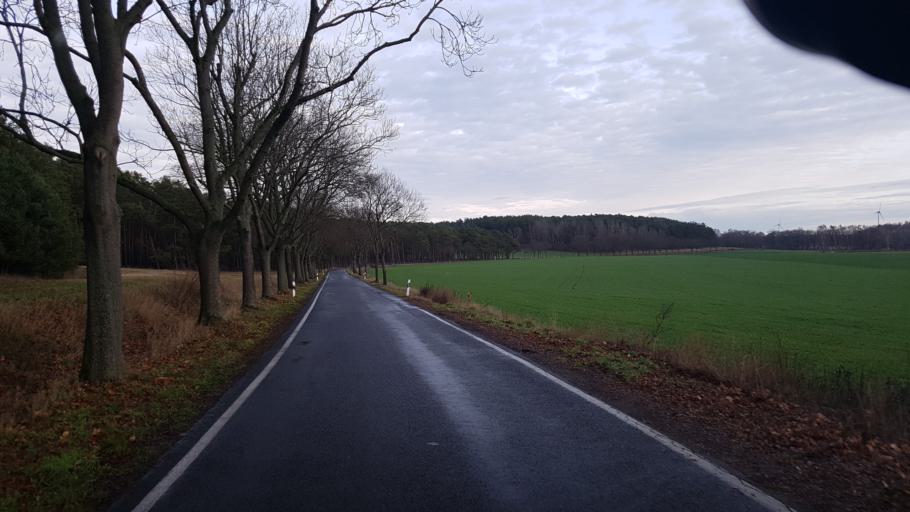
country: DE
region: Brandenburg
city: Hohenbucko
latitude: 51.7419
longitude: 13.4454
